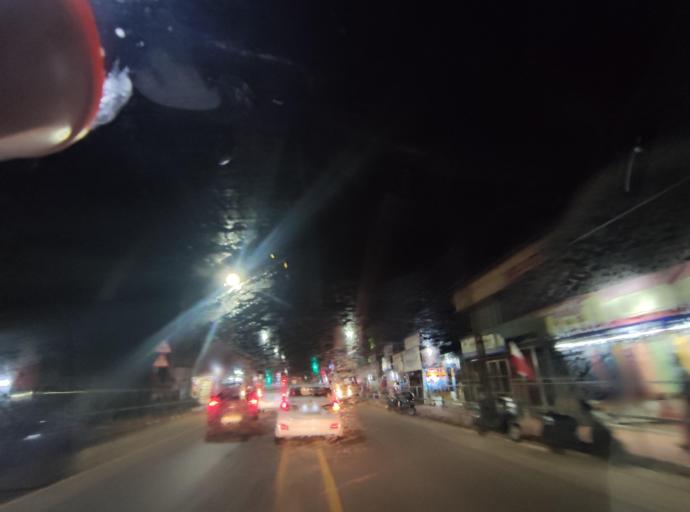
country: IN
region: Kerala
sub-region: Thiruvananthapuram
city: Attingal
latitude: 8.7303
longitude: 76.8985
